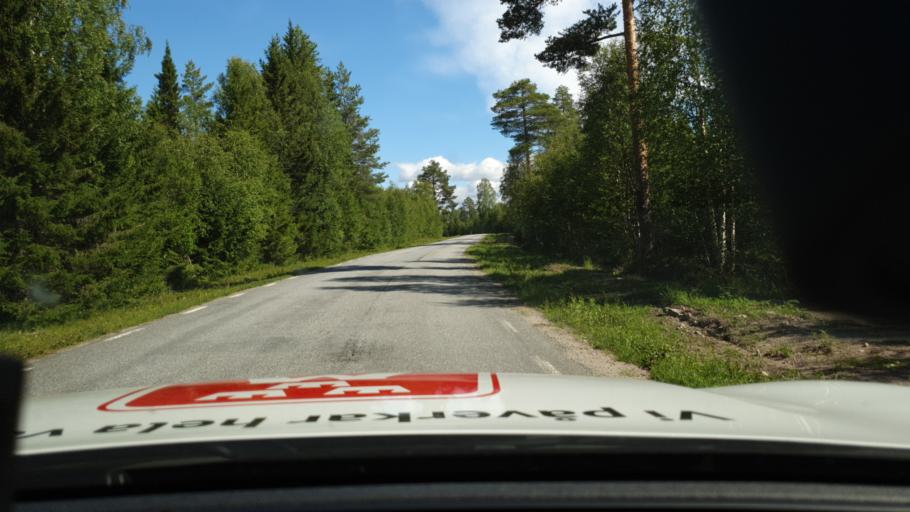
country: SE
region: Norrbotten
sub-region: Lulea Kommun
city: Ranea
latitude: 65.8216
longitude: 22.3141
